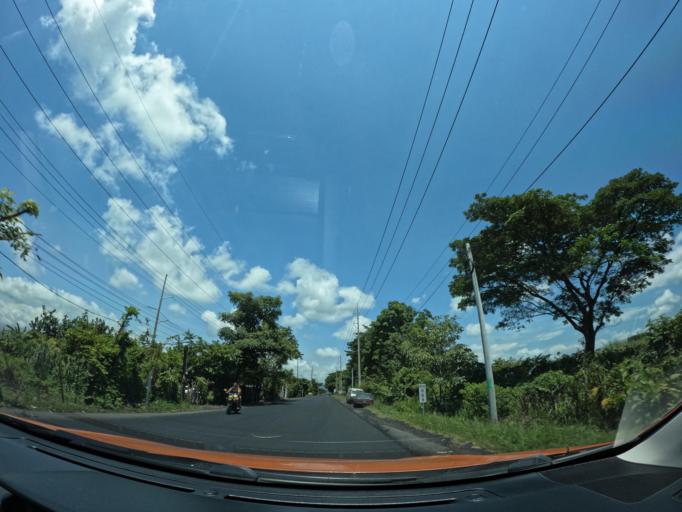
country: GT
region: Escuintla
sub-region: Municipio de Masagua
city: Masagua
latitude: 14.2120
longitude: -90.8379
